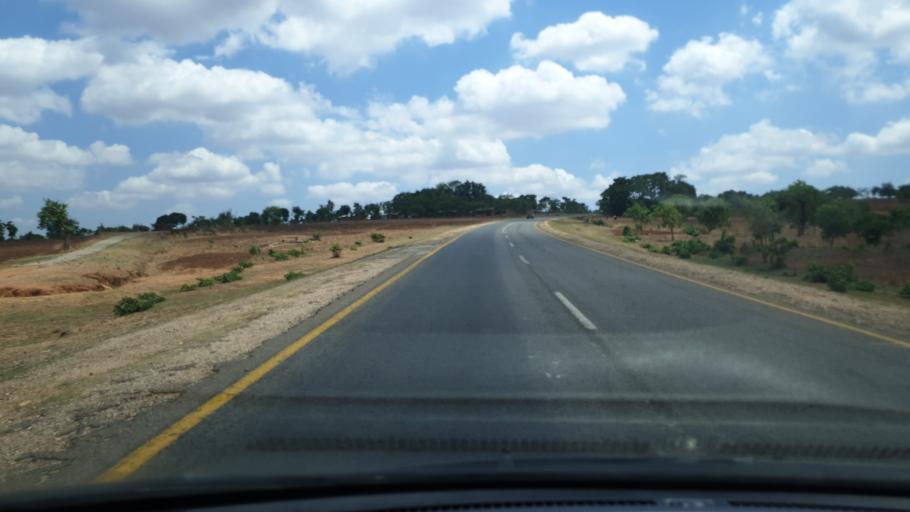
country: MW
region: Central Region
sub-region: Dowa District
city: Dowa
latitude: -13.7751
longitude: 34.0038
